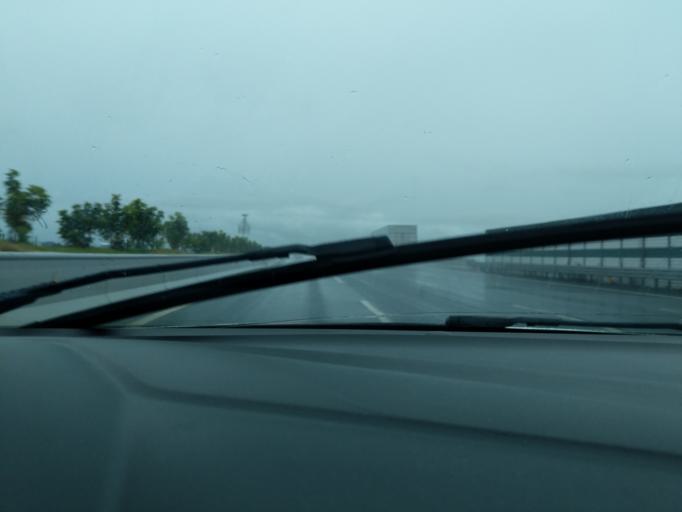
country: CN
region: Guangdong
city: Zhishan
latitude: 22.4858
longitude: 112.7924
